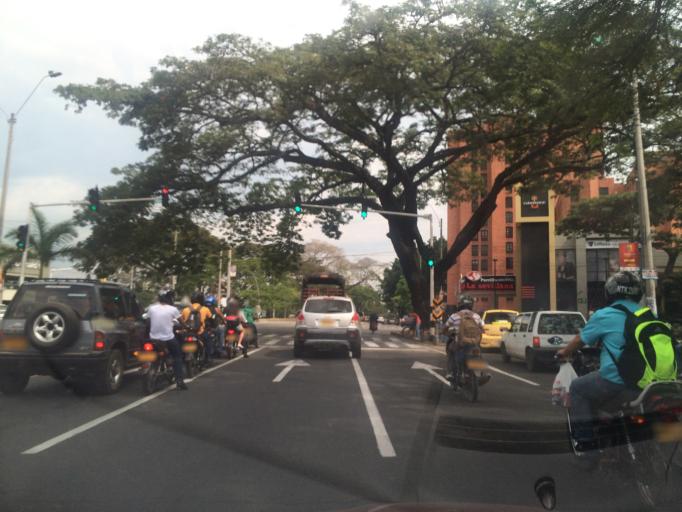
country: CO
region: Valle del Cauca
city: Cali
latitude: 3.4094
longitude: -76.5475
